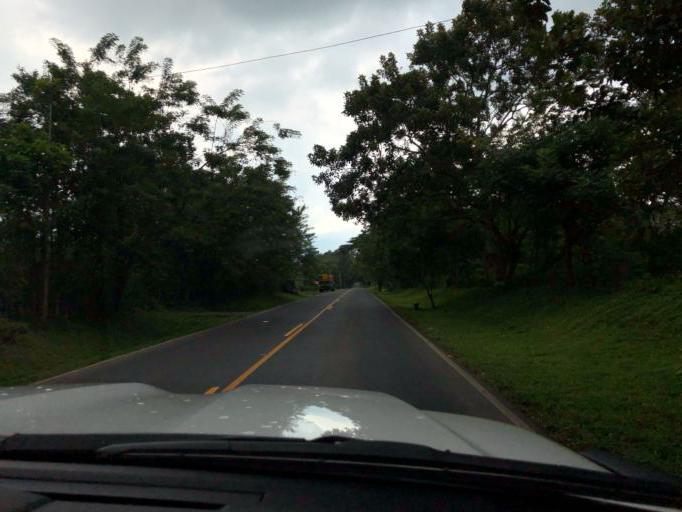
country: NI
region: Chontales
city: Villa Sandino
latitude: 11.9938
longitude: -84.8012
